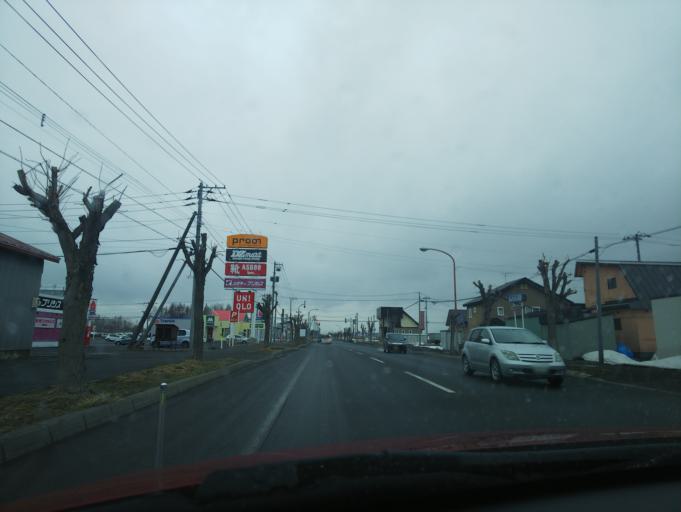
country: JP
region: Hokkaido
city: Nayoro
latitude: 44.3374
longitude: 142.4503
